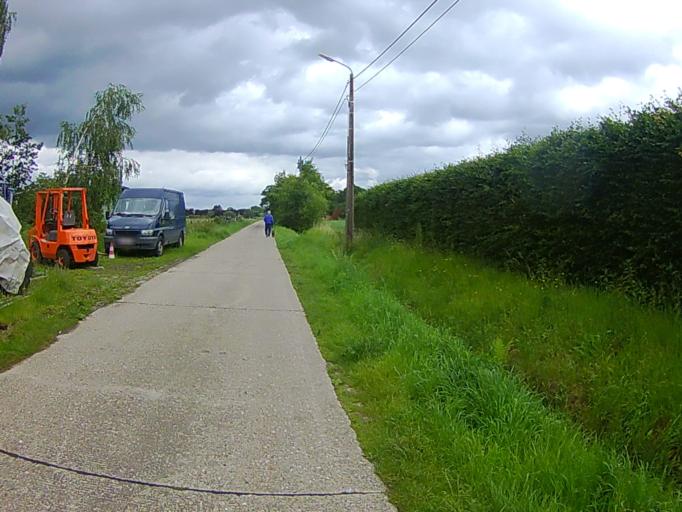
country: BE
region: Flanders
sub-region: Provincie Antwerpen
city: Heist-op-den-Berg
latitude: 51.1053
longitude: 4.7119
